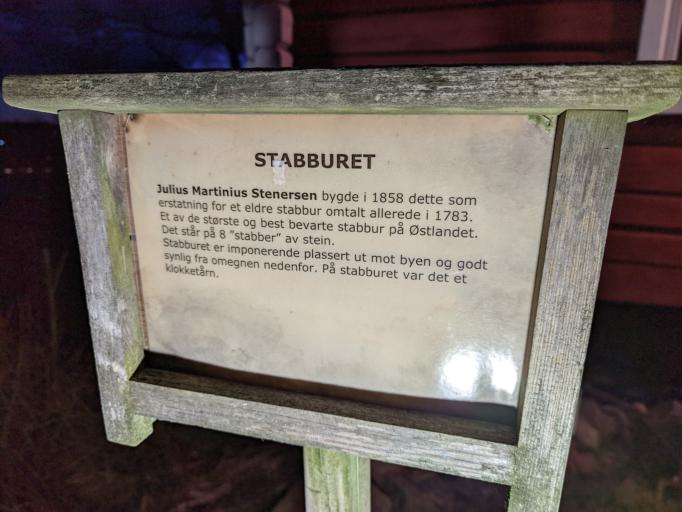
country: NO
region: Oslo
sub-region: Oslo
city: Oslo
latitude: 59.9136
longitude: 10.8358
